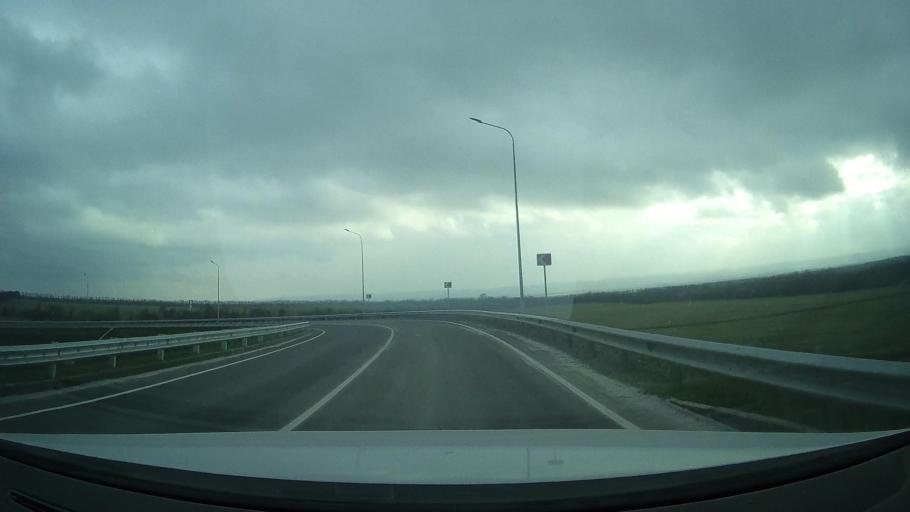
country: RU
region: Rostov
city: Grushevskaya
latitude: 47.4939
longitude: 39.9511
